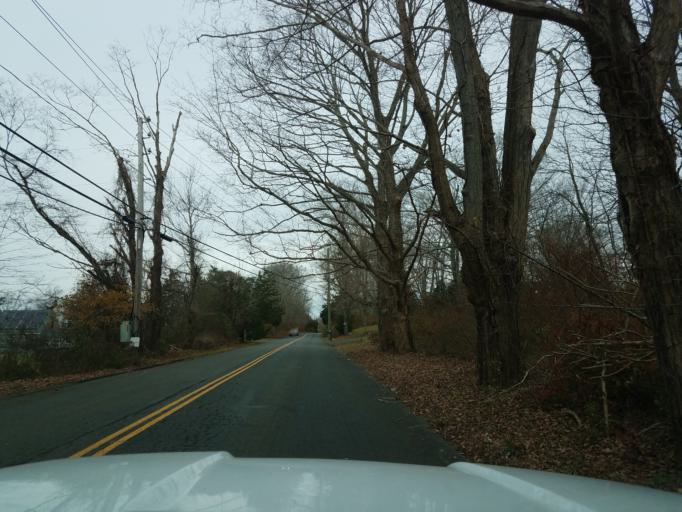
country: US
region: Connecticut
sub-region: New Haven County
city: Guilford
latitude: 41.3185
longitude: -72.7100
